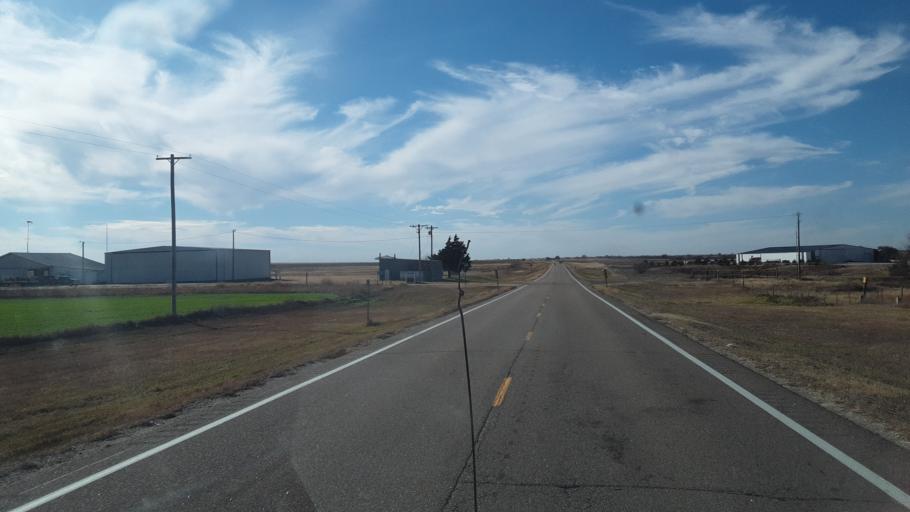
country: US
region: Kansas
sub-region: Edwards County
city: Kinsley
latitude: 38.1897
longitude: -99.5323
